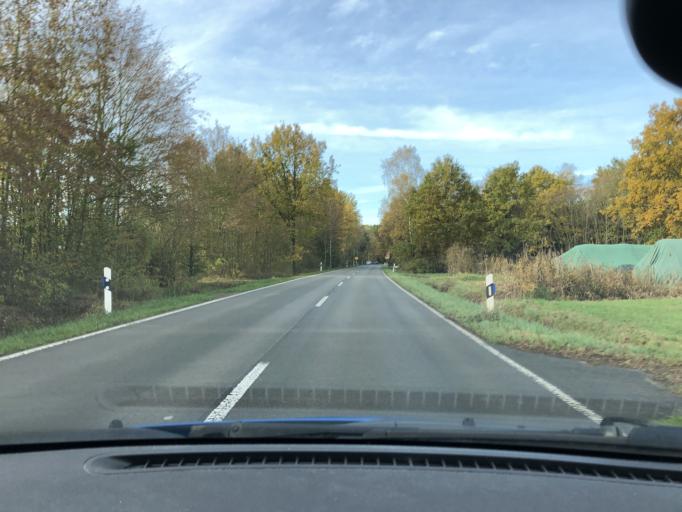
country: DE
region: Lower Saxony
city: Tespe
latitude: 53.3889
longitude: 10.4314
